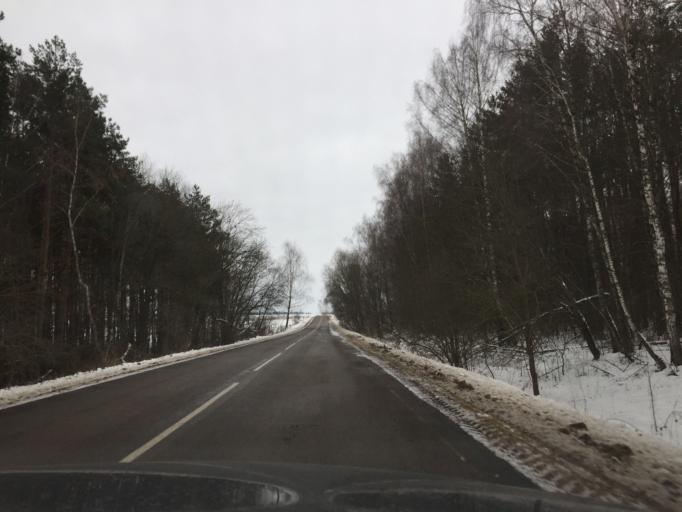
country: RU
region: Tula
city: Teploye
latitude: 53.8096
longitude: 37.5429
